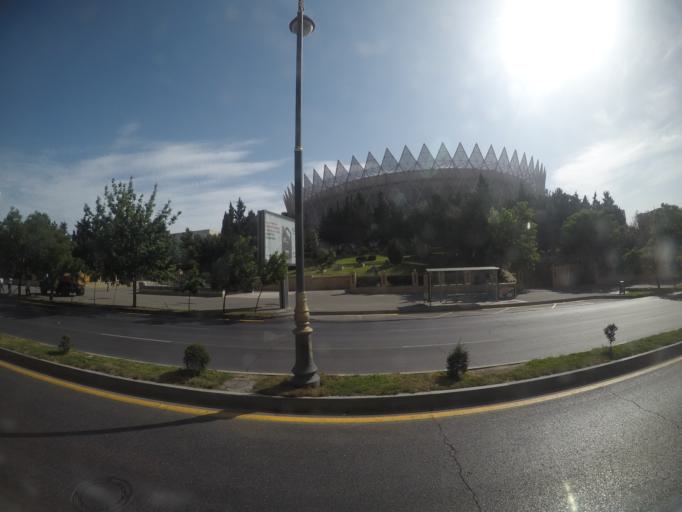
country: AZ
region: Baki
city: Badamdar
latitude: 40.3911
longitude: 49.8236
